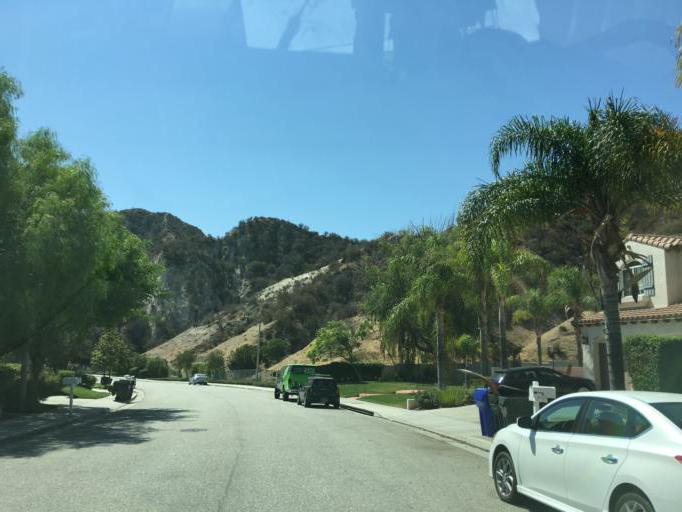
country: US
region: California
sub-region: Los Angeles County
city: Santa Clarita
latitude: 34.3852
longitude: -118.6007
